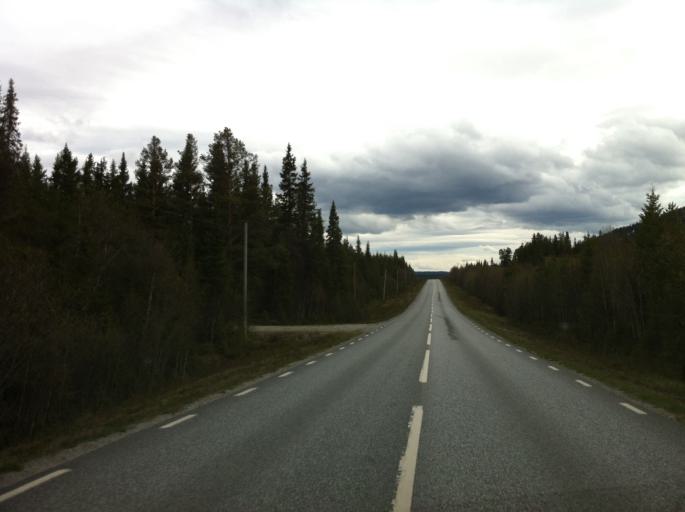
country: SE
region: Jaemtland
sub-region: Are Kommun
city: Are
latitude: 62.6013
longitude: 12.5206
